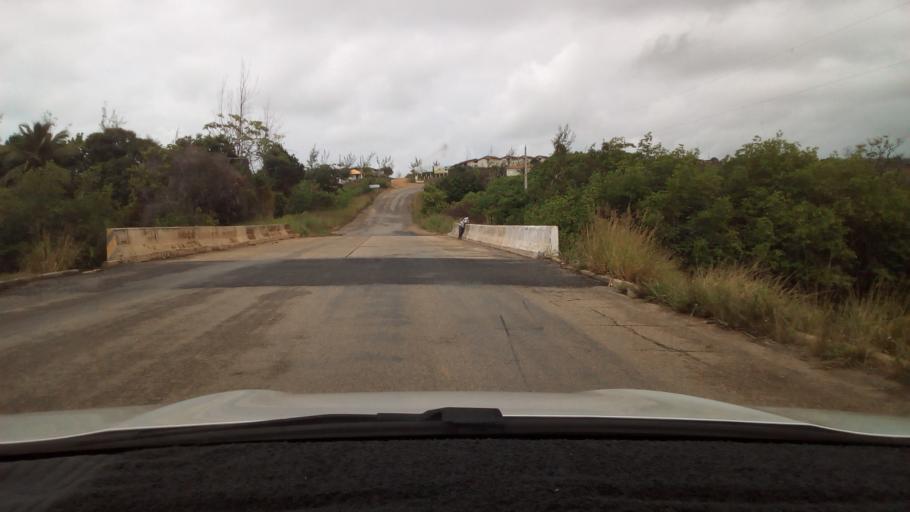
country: BR
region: Paraiba
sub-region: Pitimbu
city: Pitimbu
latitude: -7.4011
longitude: -34.8112
